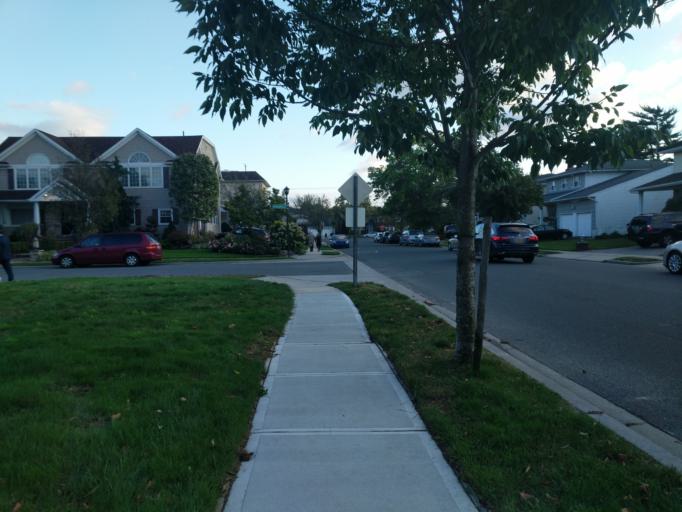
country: US
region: New York
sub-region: Nassau County
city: South Valley Stream
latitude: 40.6457
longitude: -73.7299
